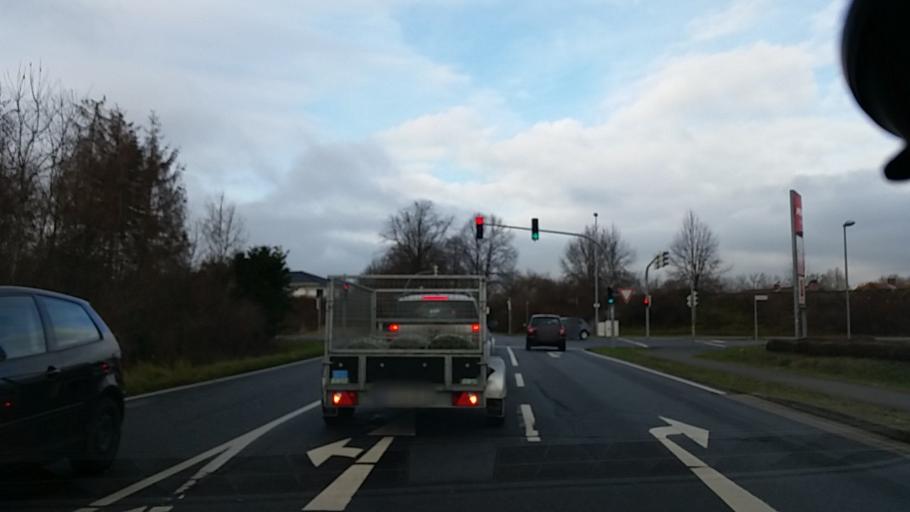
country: DE
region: Lower Saxony
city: Wolfsburg
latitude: 52.4492
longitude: 10.8343
